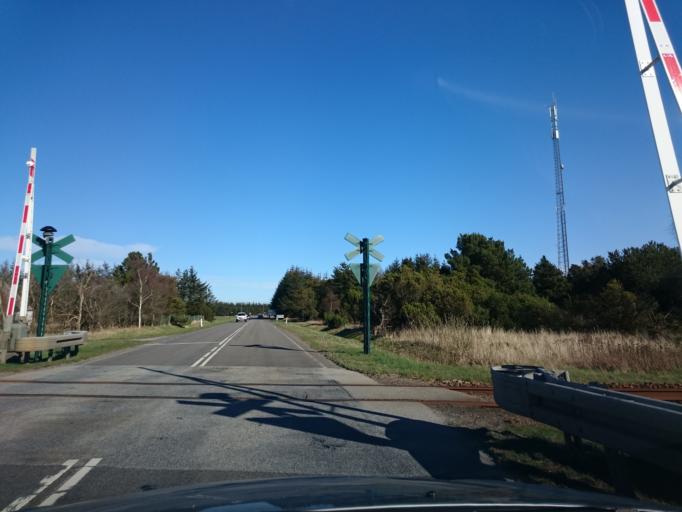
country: DK
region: North Denmark
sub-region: Frederikshavn Kommune
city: Strandby
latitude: 57.6061
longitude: 10.4176
